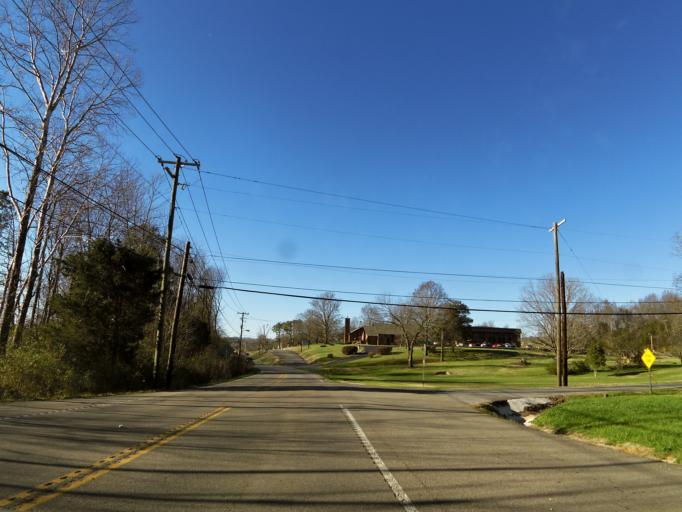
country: US
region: Tennessee
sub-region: Knox County
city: Knoxville
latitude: 36.0359
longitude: -83.9989
